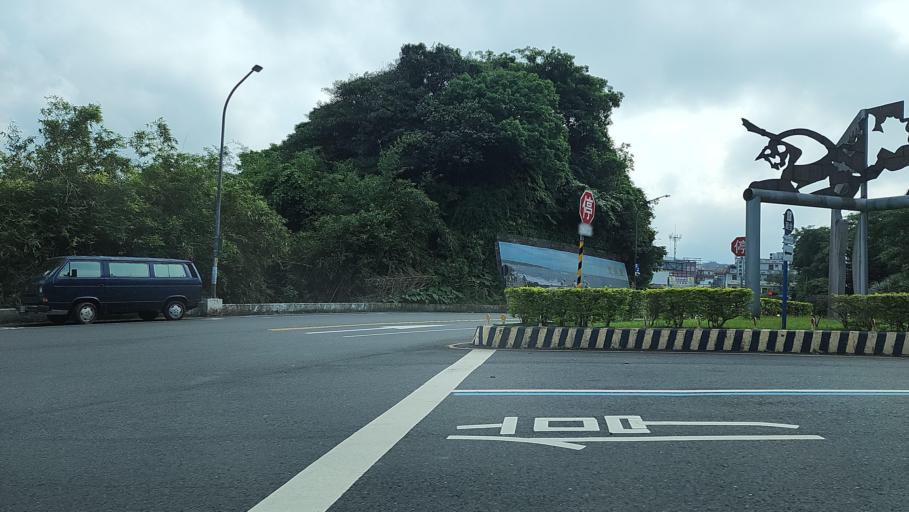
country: TW
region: Taiwan
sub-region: Keelung
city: Keelung
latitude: 25.2214
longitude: 121.6430
